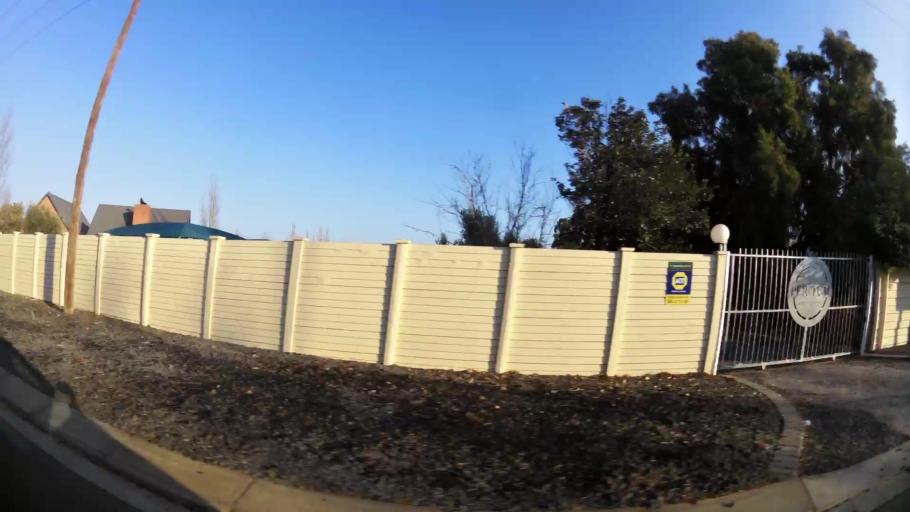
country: ZA
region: Orange Free State
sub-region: Mangaung Metropolitan Municipality
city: Bloemfontein
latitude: -29.0817
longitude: 26.1473
